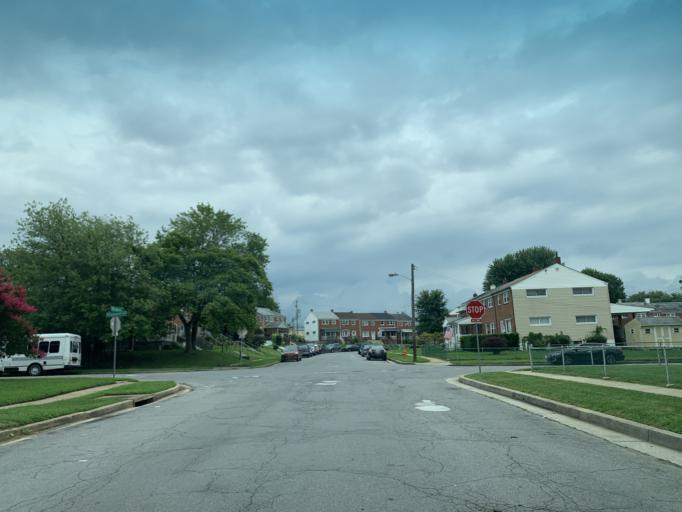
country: US
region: Maryland
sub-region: Baltimore County
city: Essex
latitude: 39.3107
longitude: -76.4502
